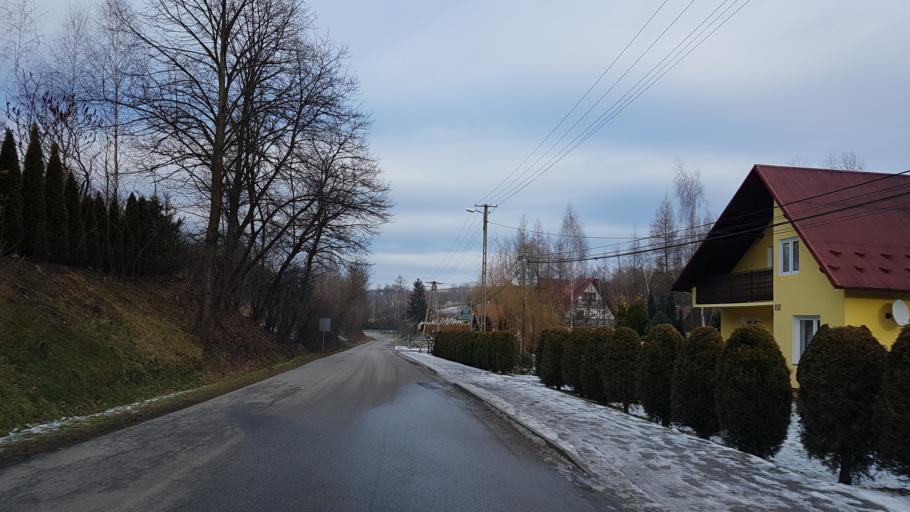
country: PL
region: Lesser Poland Voivodeship
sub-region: Powiat nowosadecki
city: Stary Sacz
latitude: 49.5333
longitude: 20.6089
